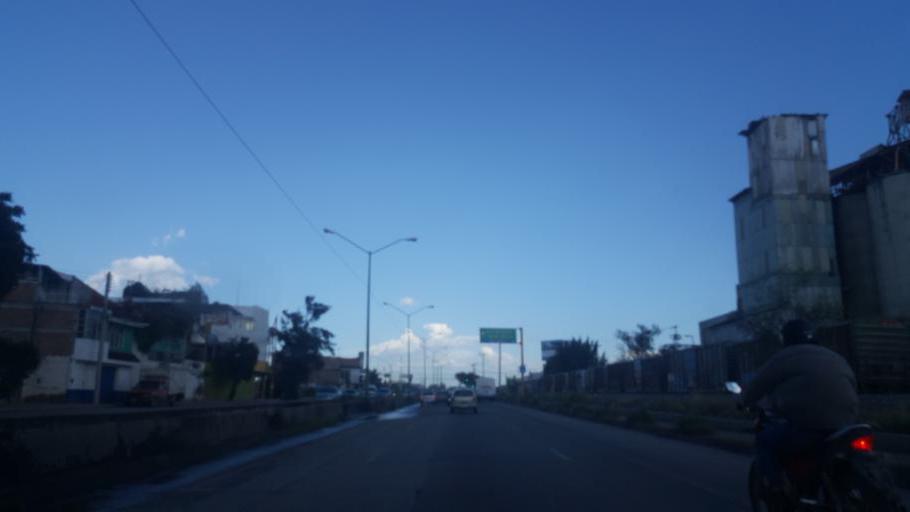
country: MX
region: Guanajuato
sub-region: Leon
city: San Jose de Duran (Los Troncoso)
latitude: 21.0855
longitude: -101.6682
